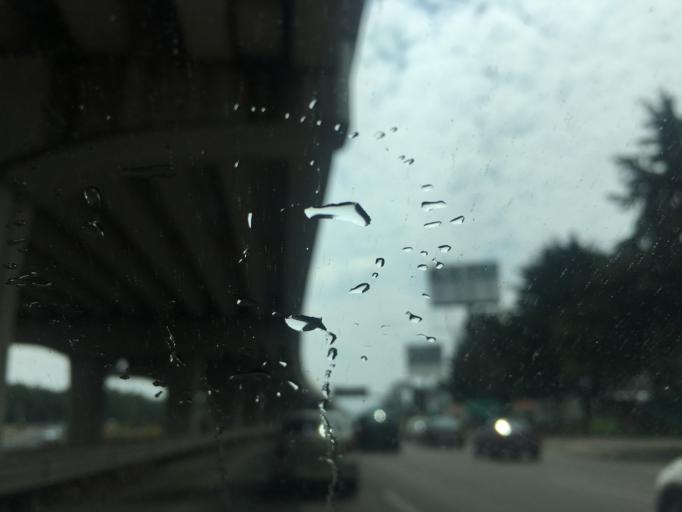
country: MX
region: Morelos
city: Ocoyoacac
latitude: 19.2888
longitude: -99.4396
